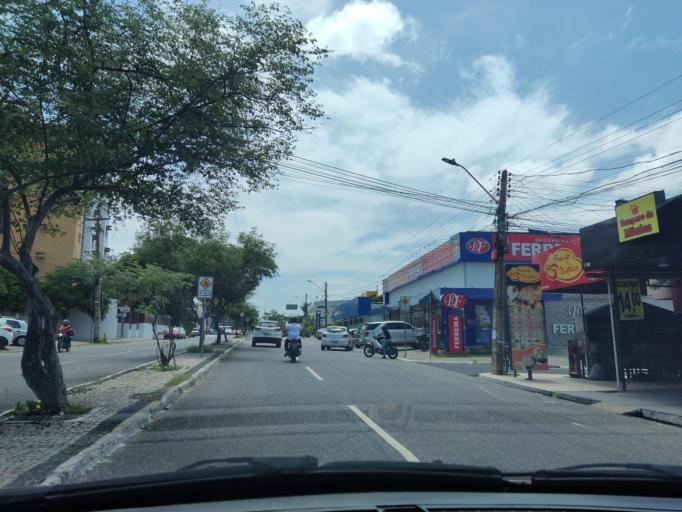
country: BR
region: Piaui
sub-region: Teresina
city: Teresina
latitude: -5.0711
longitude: -42.7629
